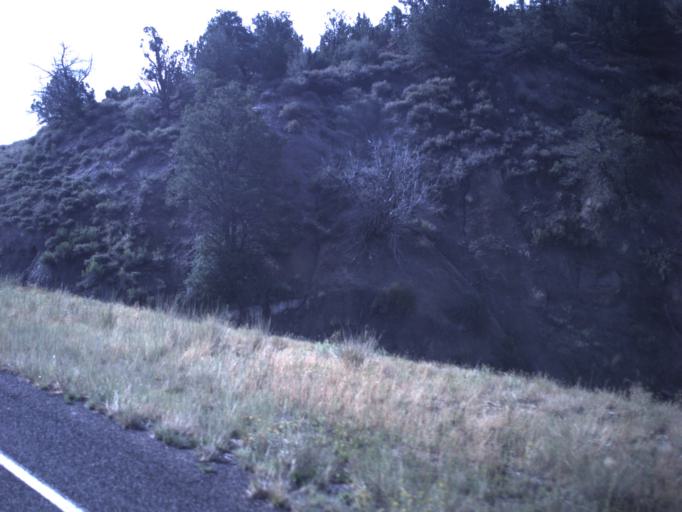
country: US
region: Utah
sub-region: Washington County
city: Hildale
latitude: 37.2628
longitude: -112.7734
